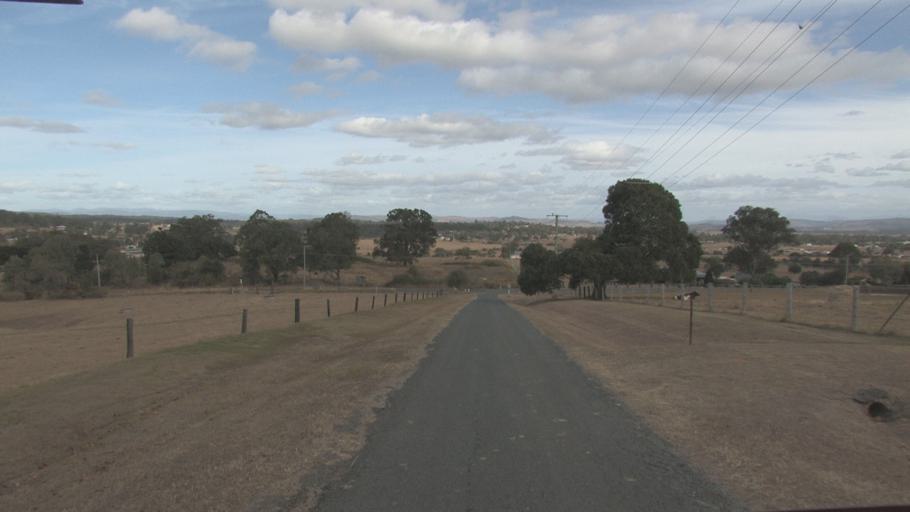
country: AU
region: Queensland
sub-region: Logan
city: Cedar Vale
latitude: -27.9143
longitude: 152.9961
